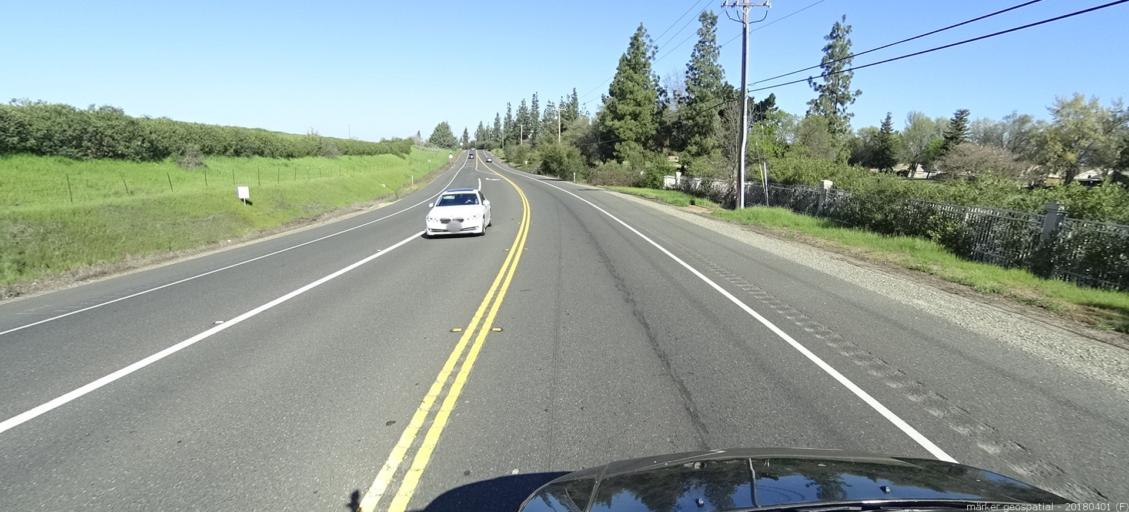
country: US
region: California
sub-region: Sacramento County
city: Rancho Murieta
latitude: 38.4879
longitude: -121.0833
